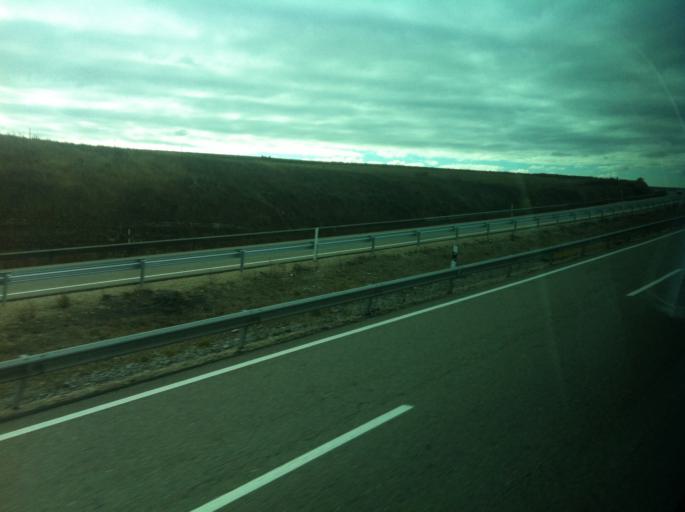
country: ES
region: Castille and Leon
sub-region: Provincia de Burgos
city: Vallarta de Bureba
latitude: 42.6145
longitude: -3.1994
